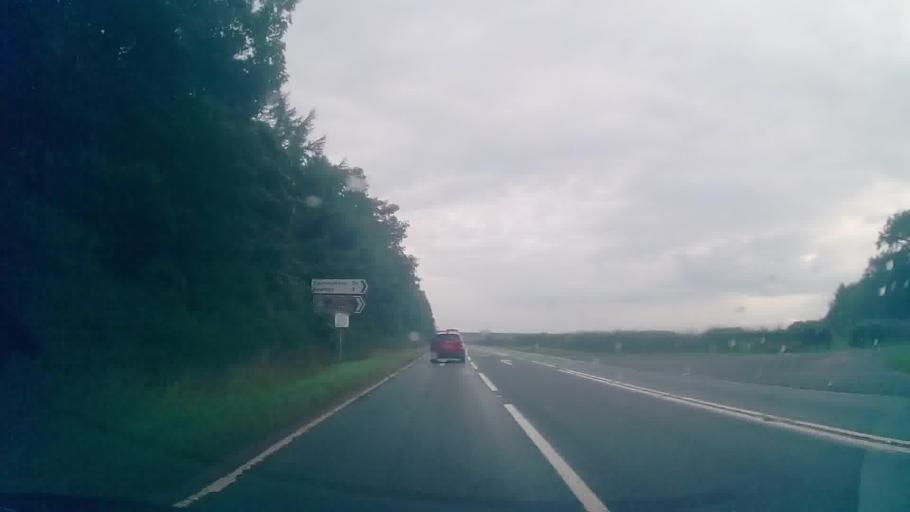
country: GB
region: Scotland
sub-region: Dumfries and Galloway
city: Annan
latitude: 55.0078
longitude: -3.3337
